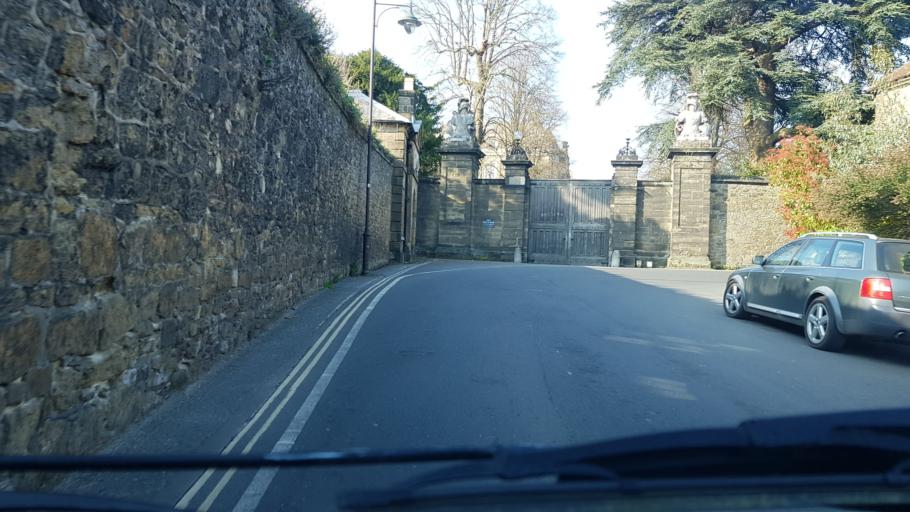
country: GB
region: England
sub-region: West Sussex
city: Petworth
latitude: 50.9866
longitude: -0.6112
